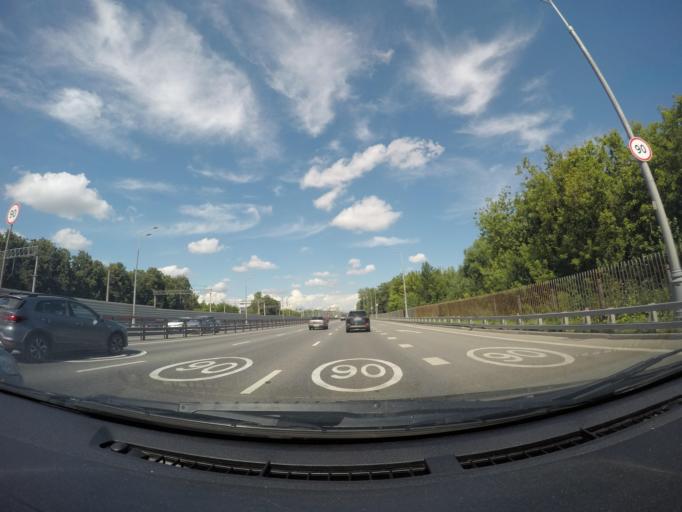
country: RU
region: Moscow
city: Perovo
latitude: 55.7255
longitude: 37.7911
